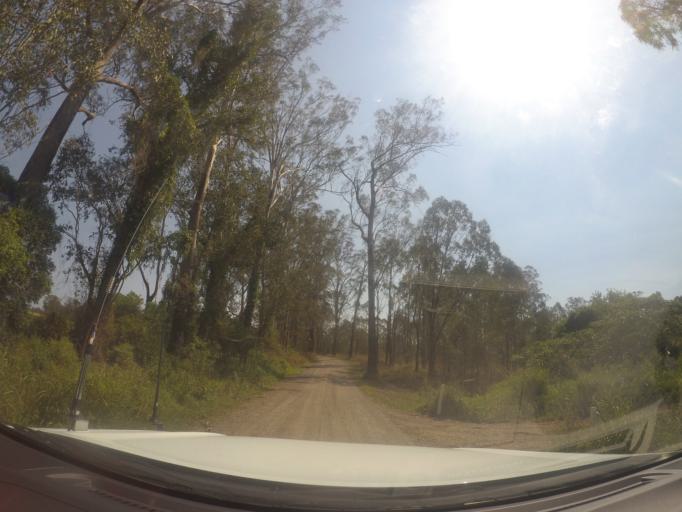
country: AU
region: Queensland
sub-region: Logan
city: North Maclean
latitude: -27.7730
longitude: 153.0384
